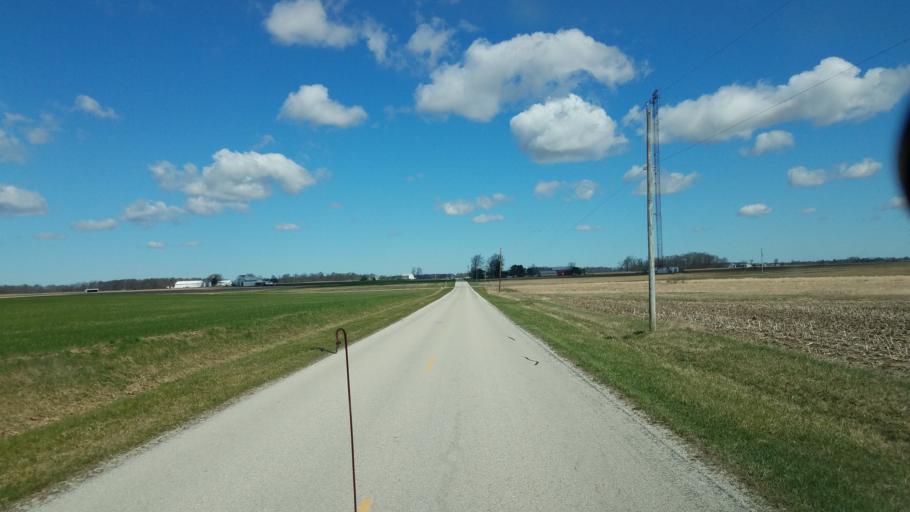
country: US
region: Ohio
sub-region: Sandusky County
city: Mount Carmel
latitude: 41.1954
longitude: -82.9375
